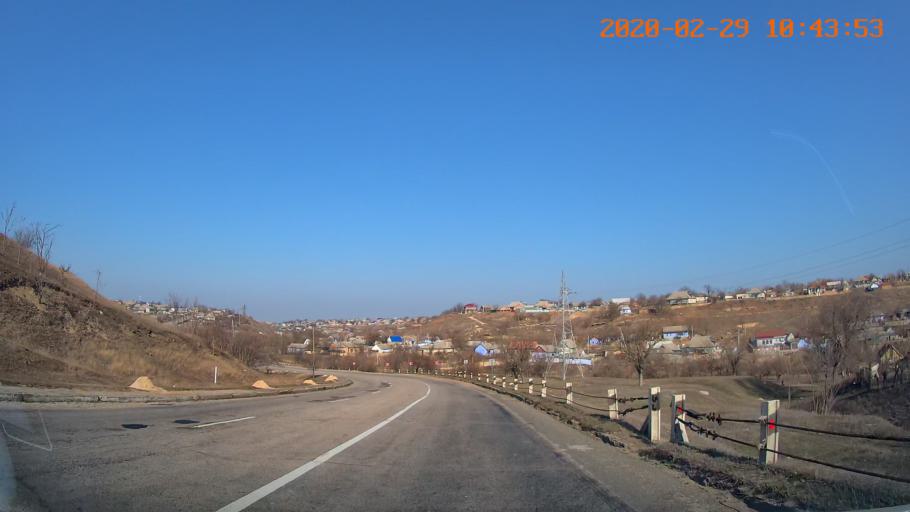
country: MD
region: Telenesti
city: Grigoriopol
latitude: 47.0664
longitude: 29.4012
